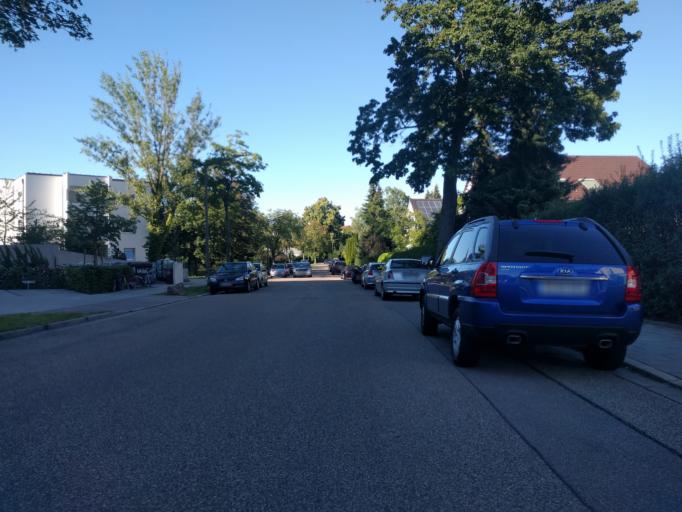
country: DE
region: Bavaria
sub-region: Upper Palatinate
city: Pentling
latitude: 49.0063
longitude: 12.0745
